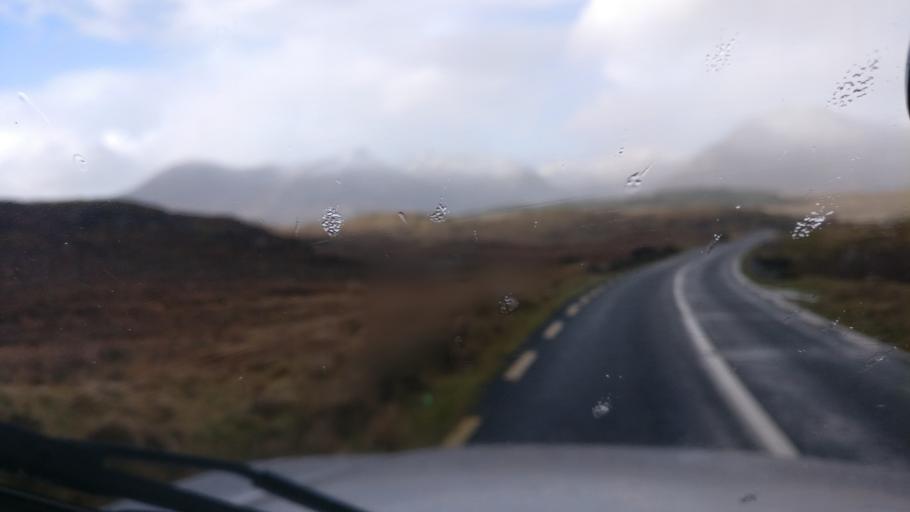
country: IE
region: Connaught
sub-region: County Galway
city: Clifden
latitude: 53.4494
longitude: -9.7719
